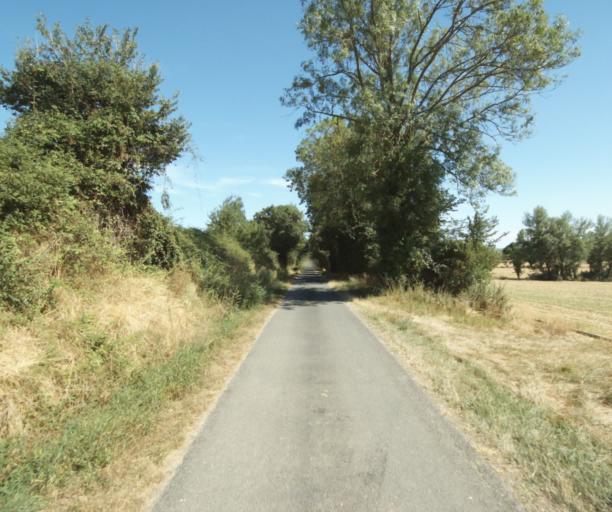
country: FR
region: Midi-Pyrenees
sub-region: Departement de la Haute-Garonne
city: Auriac-sur-Vendinelle
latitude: 43.5223
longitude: 1.8880
